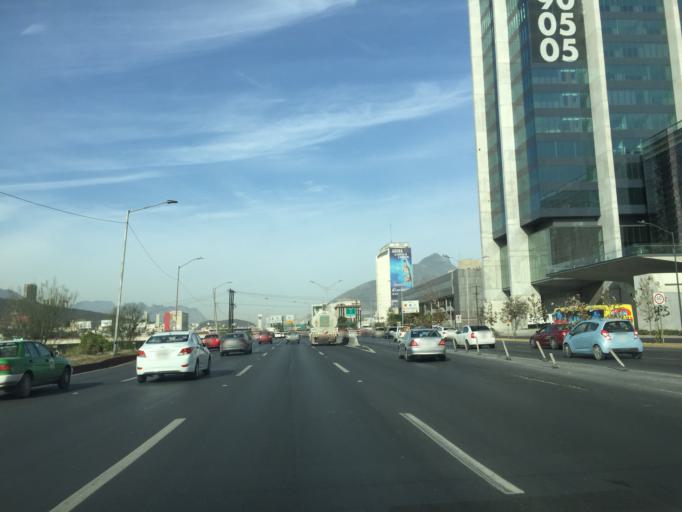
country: MX
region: Nuevo Leon
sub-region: Monterrey
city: Monterrey
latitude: 25.6646
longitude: -100.3164
